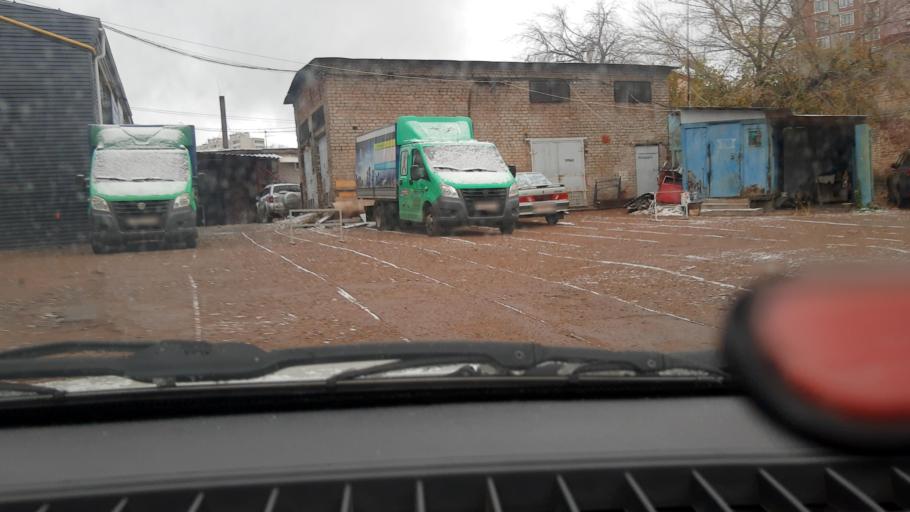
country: RU
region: Bashkortostan
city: Ufa
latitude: 54.7240
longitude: 55.9817
